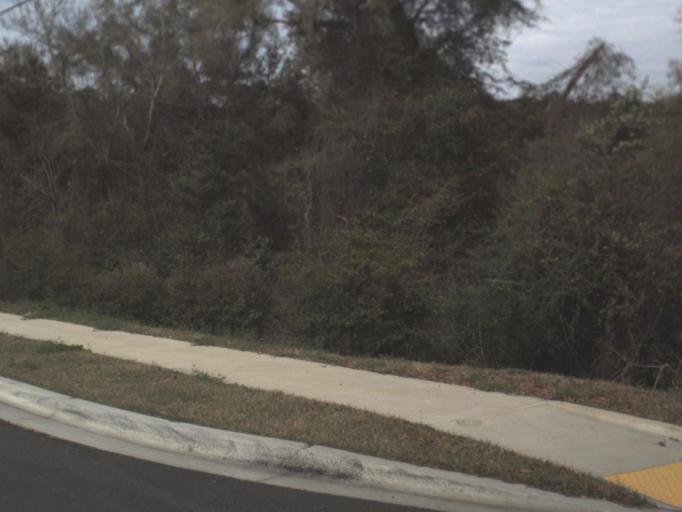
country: US
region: Florida
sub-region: Leon County
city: Tallahassee
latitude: 30.4783
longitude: -84.1776
